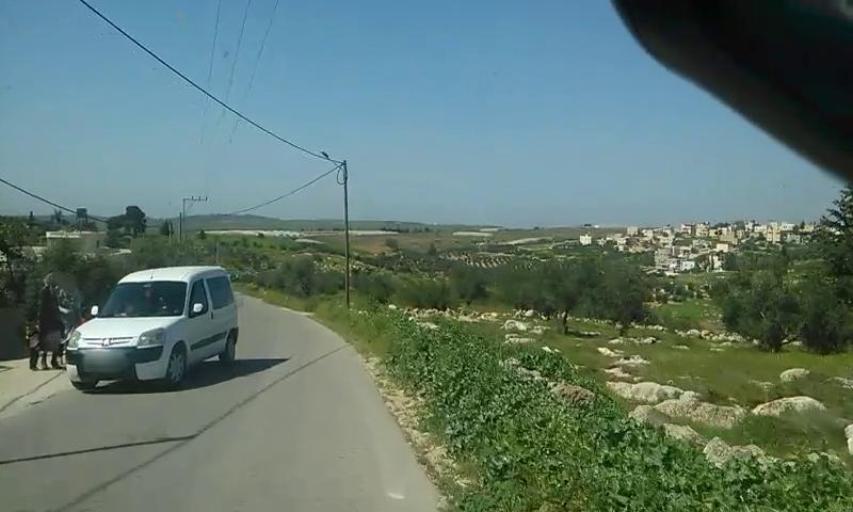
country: PS
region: West Bank
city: Al Majd
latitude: 31.4858
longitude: 34.9444
